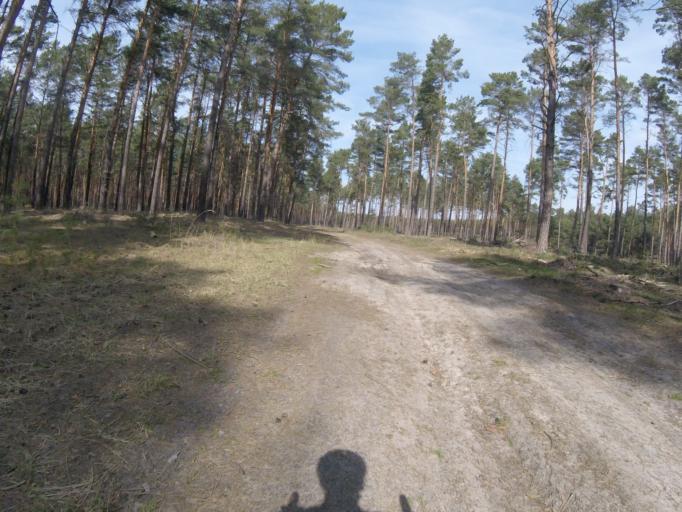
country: DE
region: Brandenburg
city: Gross Koris
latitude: 52.2043
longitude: 13.6645
